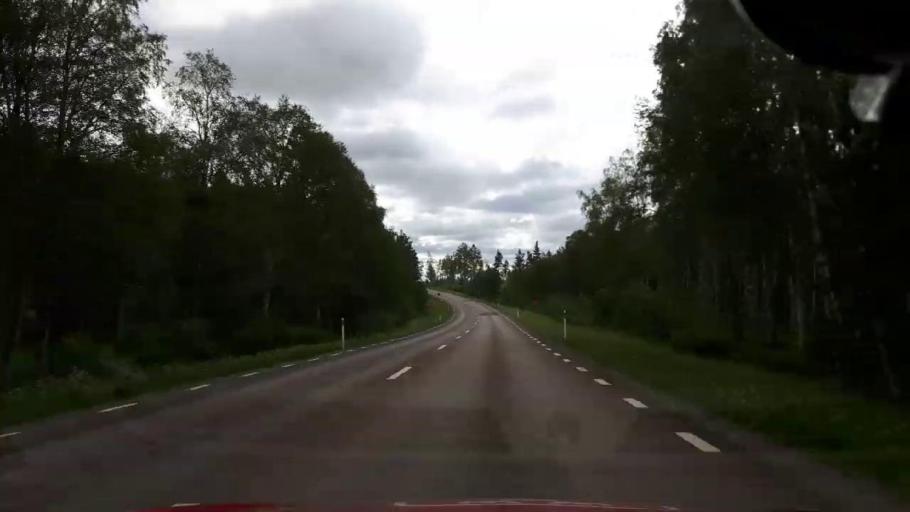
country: SE
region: Jaemtland
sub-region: OEstersunds Kommun
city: Brunflo
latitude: 63.0229
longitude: 14.9227
